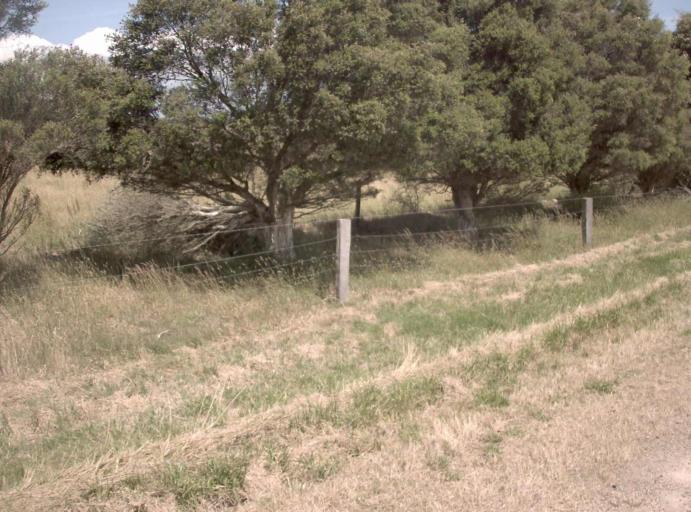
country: AU
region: Victoria
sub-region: Wellington
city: Heyfield
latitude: -38.0625
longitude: 146.8725
